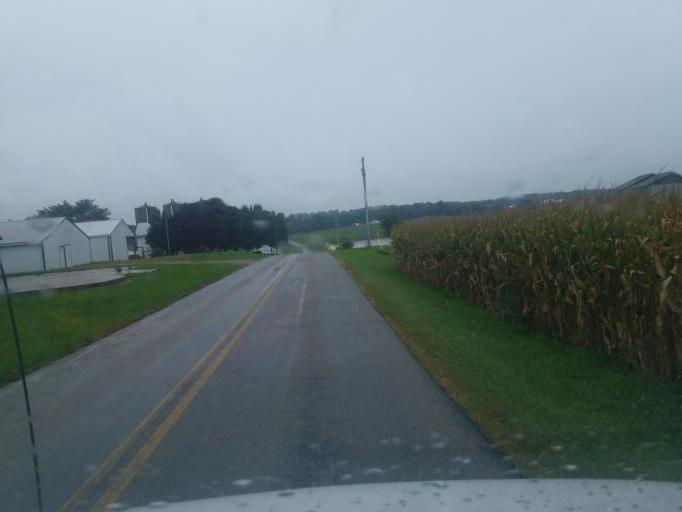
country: US
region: Ohio
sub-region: Wayne County
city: Rittman
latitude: 40.9782
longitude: -81.8216
